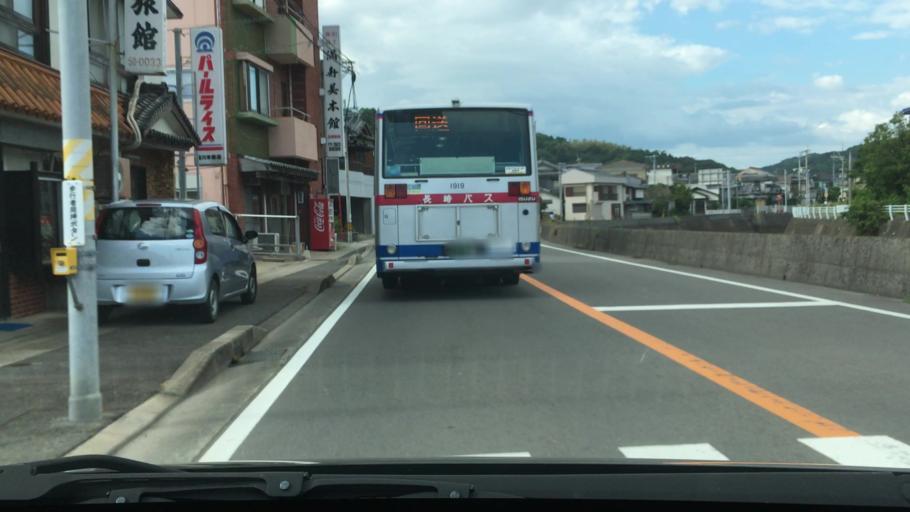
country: JP
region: Nagasaki
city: Togitsu
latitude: 32.8236
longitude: 129.7494
